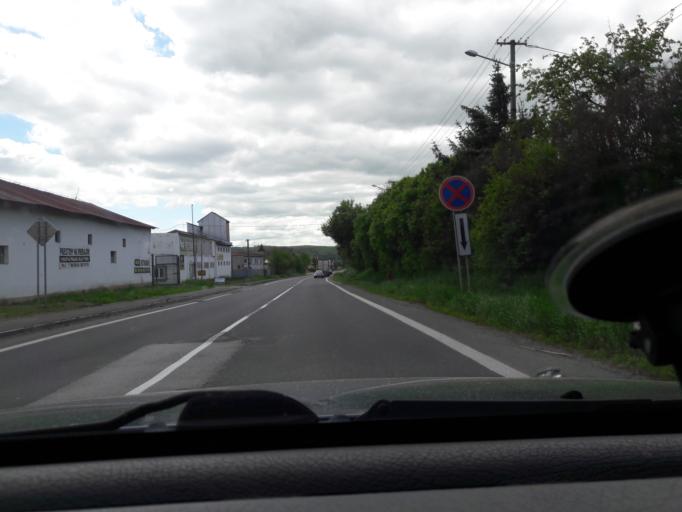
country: SK
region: Banskobystricky
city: Krupina
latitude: 48.3463
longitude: 19.0665
